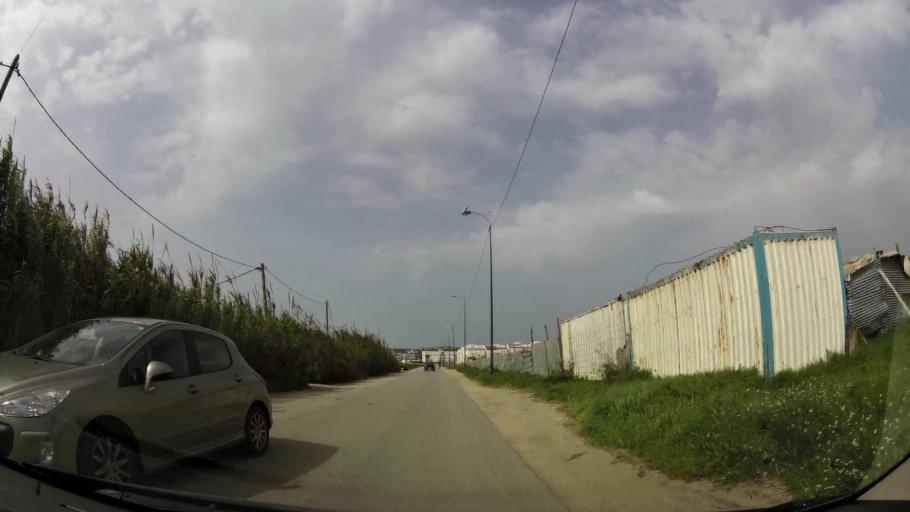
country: MA
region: Tanger-Tetouan
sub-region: Tanger-Assilah
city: Boukhalef
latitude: 35.7299
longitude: -5.8958
